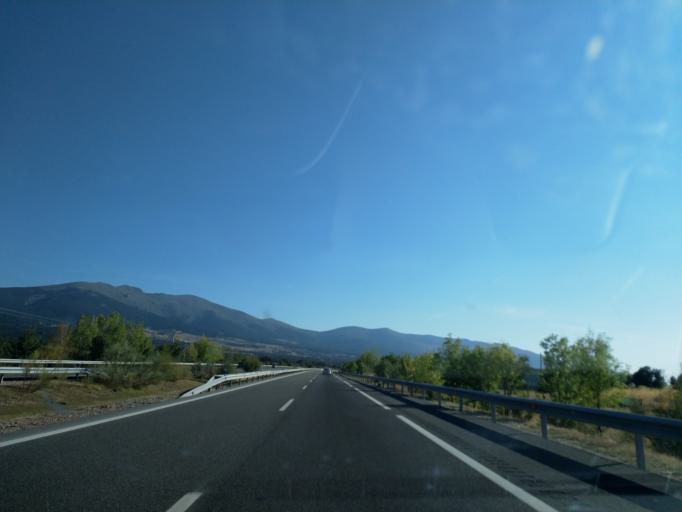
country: ES
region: Castille and Leon
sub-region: Provincia de Segovia
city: Segovia
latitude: 40.8849
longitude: -4.1171
